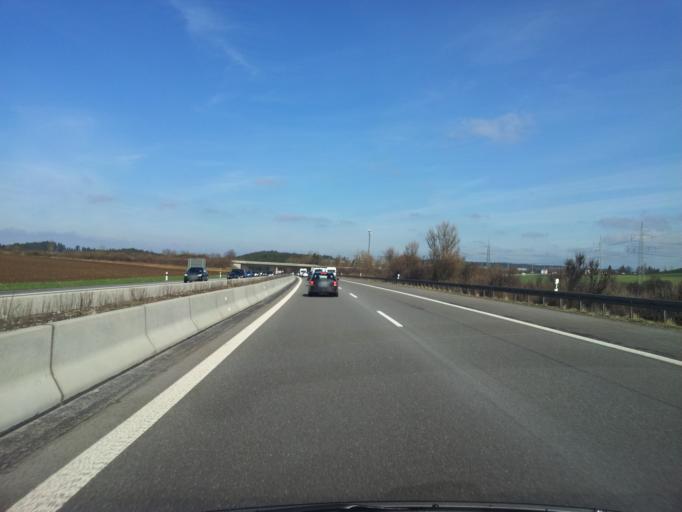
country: DE
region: Baden-Wuerttemberg
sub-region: Freiburg Region
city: Trossingen
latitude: 48.0577
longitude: 8.6205
